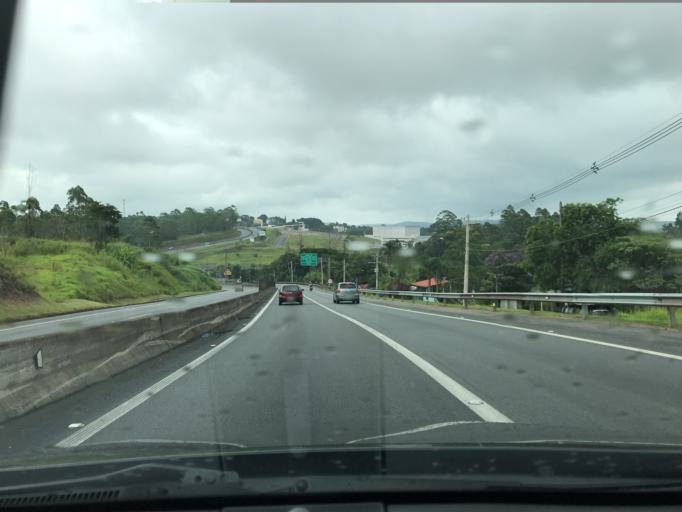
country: BR
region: Sao Paulo
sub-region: Vargem Grande Paulista
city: Vargem Grande Paulista
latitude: -23.6124
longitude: -46.9845
